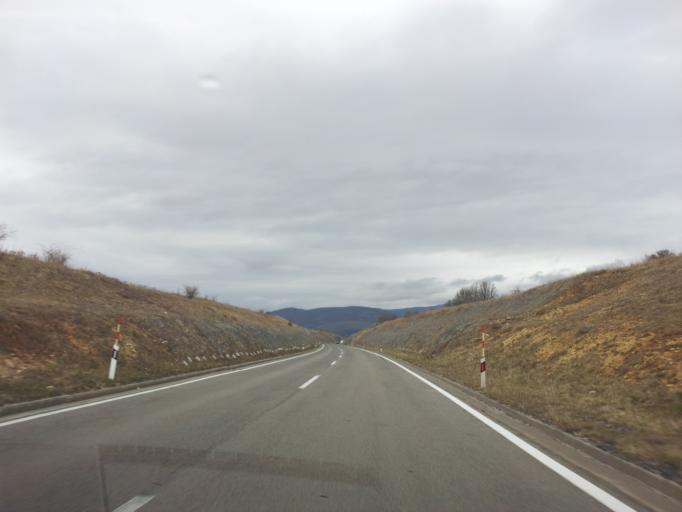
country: HR
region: Zadarska
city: Gracac
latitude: 44.5294
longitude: 15.7496
